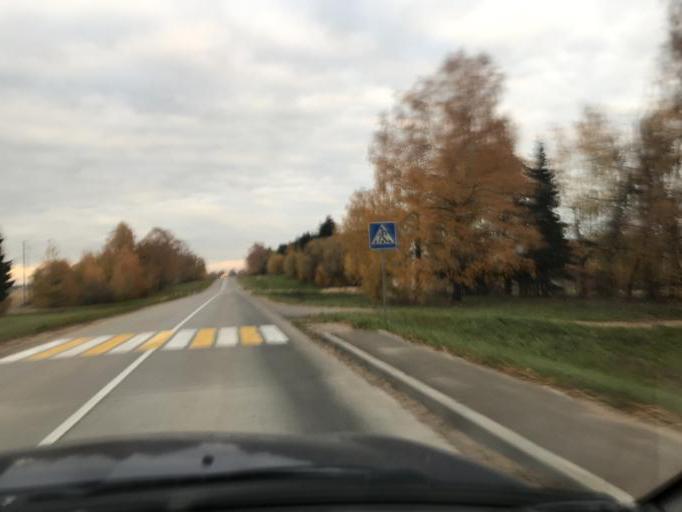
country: BY
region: Minsk
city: Hatava
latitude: 53.7676
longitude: 27.6236
